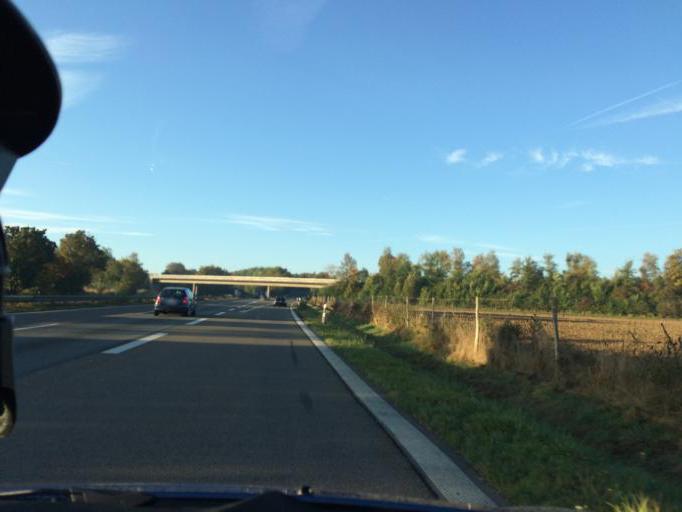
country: DE
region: North Rhine-Westphalia
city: Meckenheim
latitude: 50.5992
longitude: 7.0358
